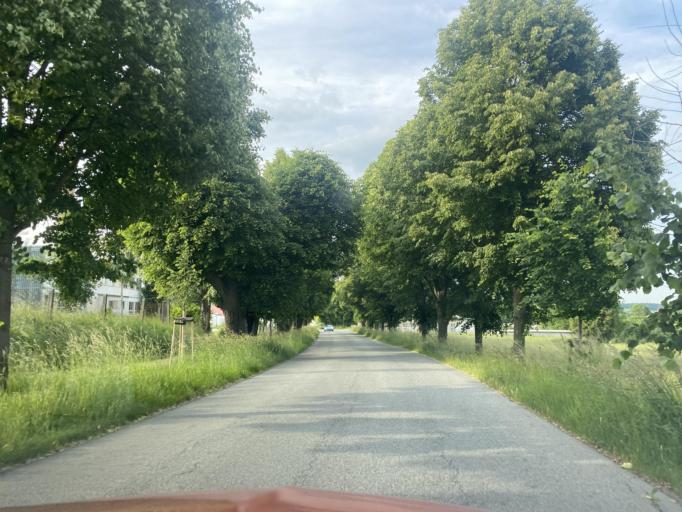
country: DE
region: Saxony
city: Herrnhut
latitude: 51.0235
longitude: 14.7594
